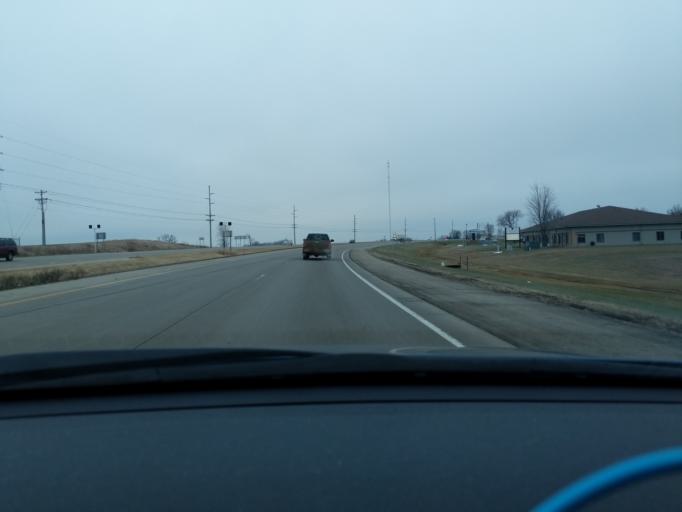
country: US
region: Minnesota
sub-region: Lyon County
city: Marshall
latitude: 44.4492
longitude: -95.7563
